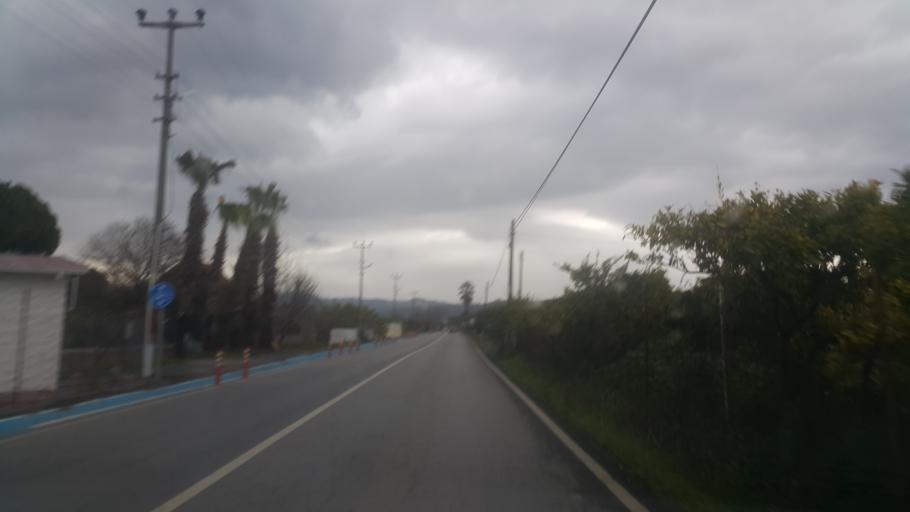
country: TR
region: Izmir
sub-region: Seferihisar
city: Seferhisar
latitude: 38.1899
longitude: 26.8147
